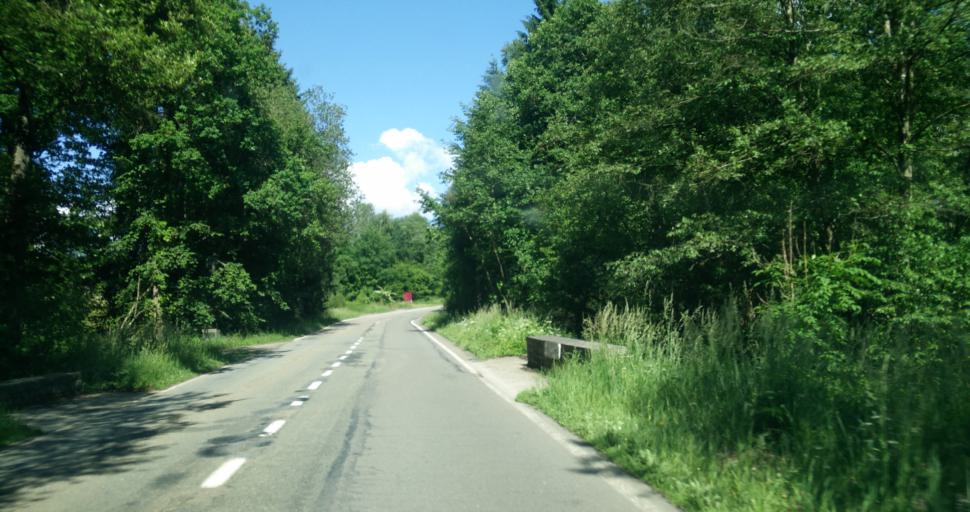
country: BE
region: Wallonia
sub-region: Province du Luxembourg
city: Rendeux
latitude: 50.1895
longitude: 5.4661
